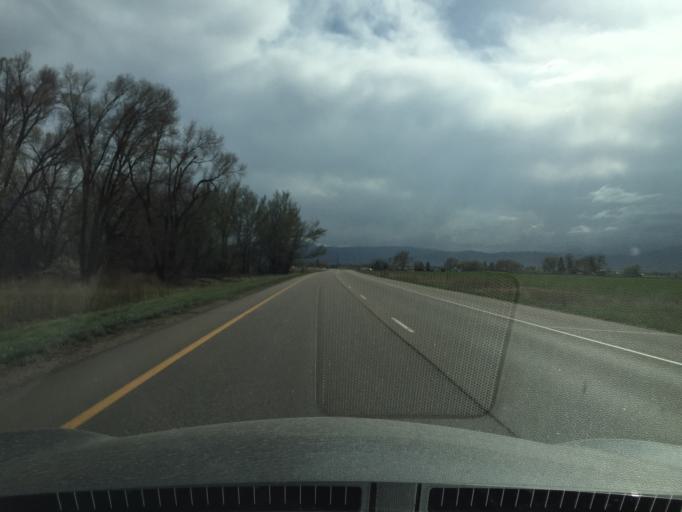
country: US
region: Colorado
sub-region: Boulder County
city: Niwot
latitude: 40.1050
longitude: -105.1739
